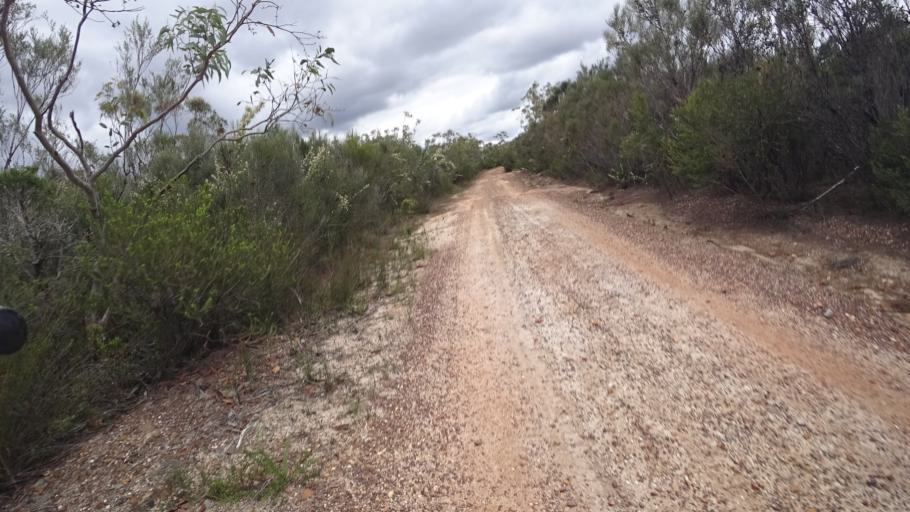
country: AU
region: New South Wales
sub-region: Shoalhaven Shire
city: Milton
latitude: -35.1255
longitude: 150.3342
